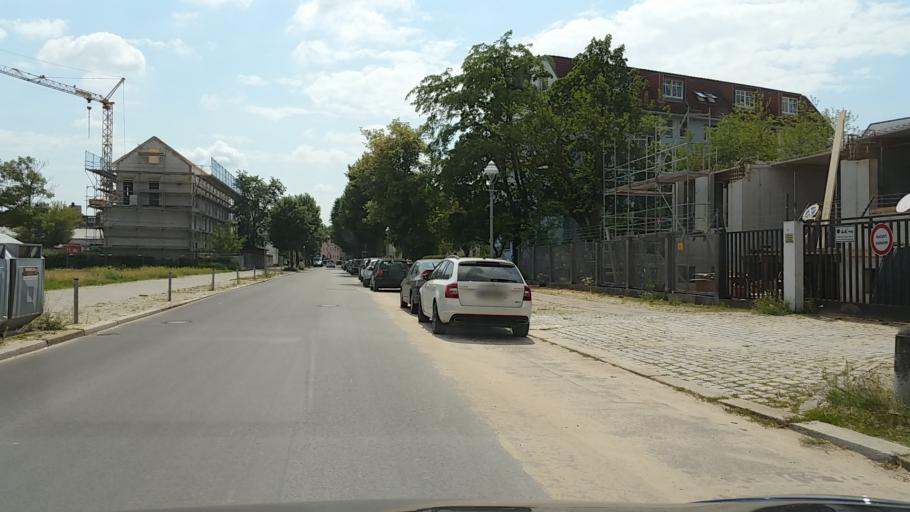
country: DE
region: Berlin
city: Hakenfelde
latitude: 52.5632
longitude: 13.2145
